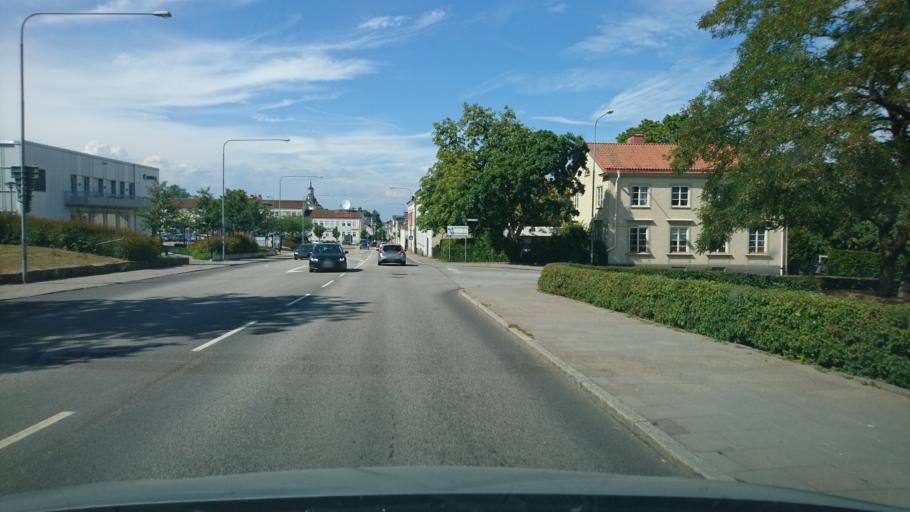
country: SE
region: Kalmar
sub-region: Vasterviks Kommun
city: Vaestervik
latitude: 57.7558
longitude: 16.6381
